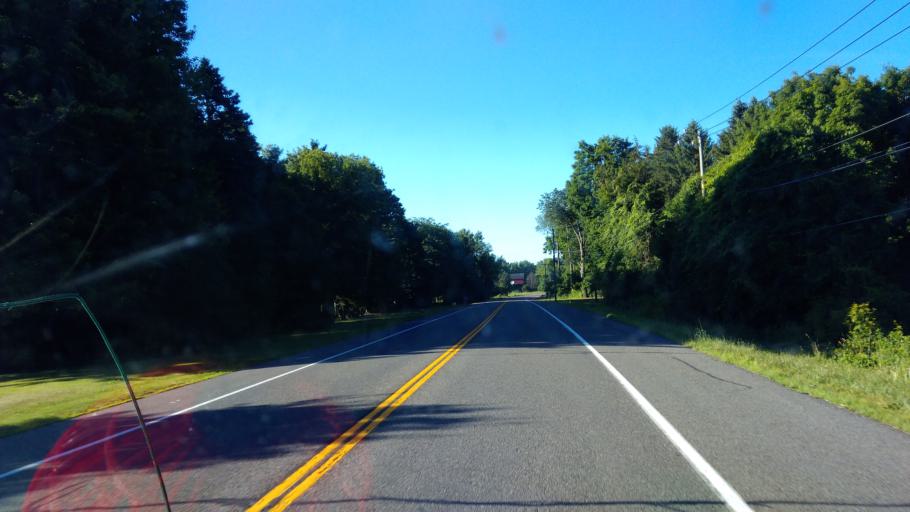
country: US
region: New York
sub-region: Ontario County
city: Phelps
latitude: 42.9622
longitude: -76.9775
